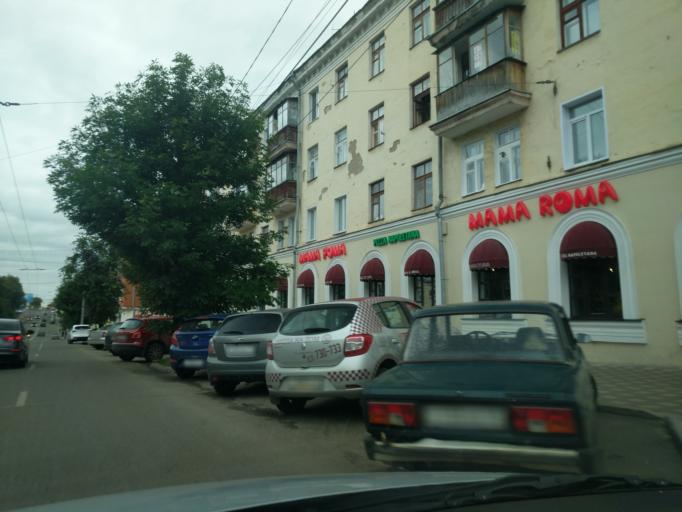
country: RU
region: Kirov
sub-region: Kirovo-Chepetskiy Rayon
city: Kirov
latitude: 58.5984
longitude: 49.6683
